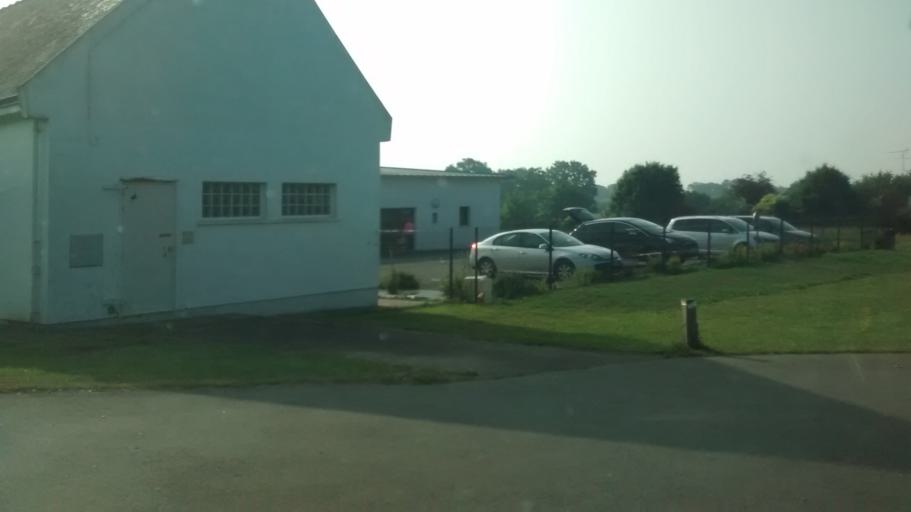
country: FR
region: Brittany
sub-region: Departement du Morbihan
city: Guer
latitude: 47.9071
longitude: -2.1221
